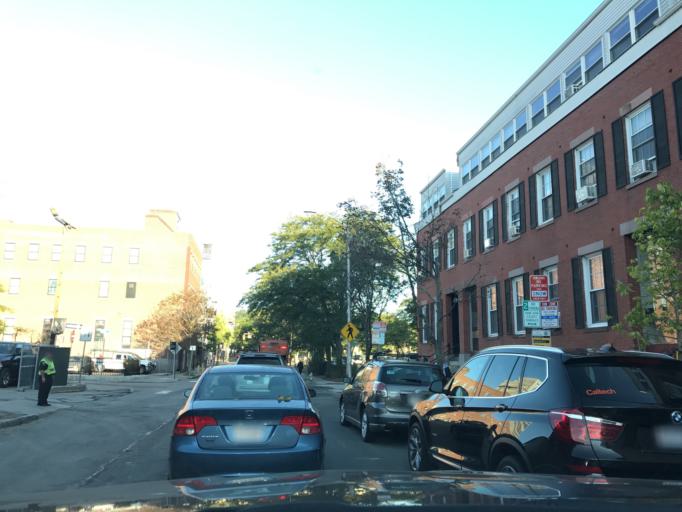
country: US
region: Massachusetts
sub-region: Middlesex County
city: Cambridge
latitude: 42.3656
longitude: -71.1019
